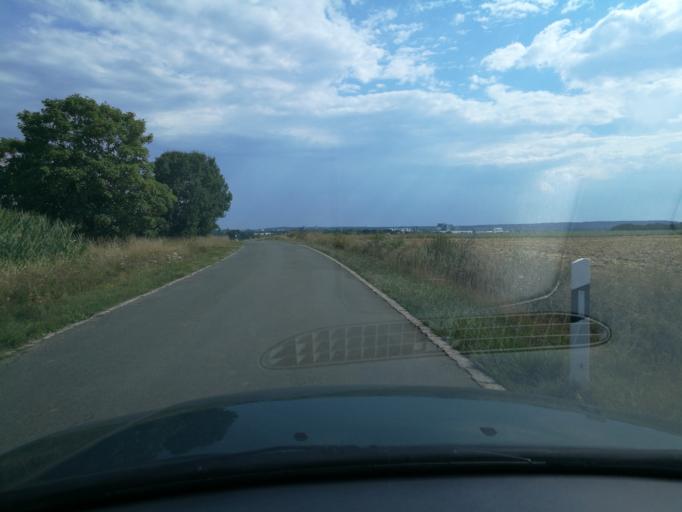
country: DE
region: Bavaria
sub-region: Regierungsbezirk Mittelfranken
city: Obermichelbach
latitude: 49.5175
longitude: 10.9525
